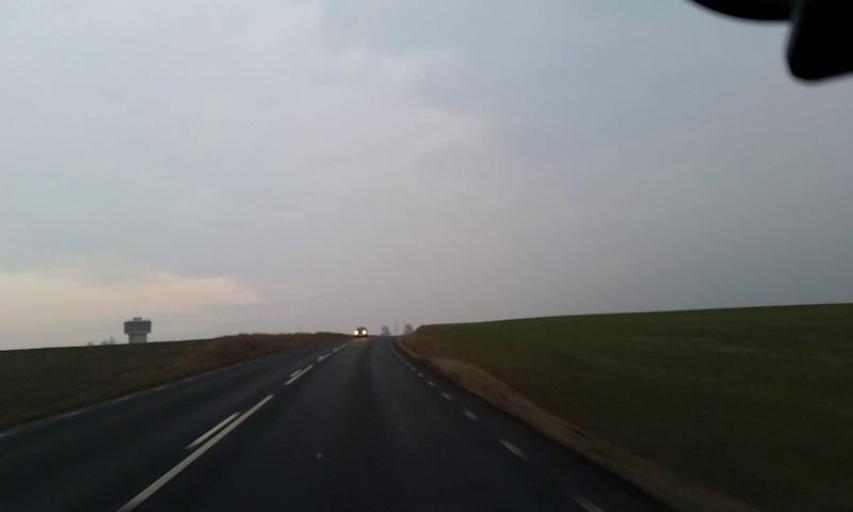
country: SE
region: Skane
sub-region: Angelholms Kommun
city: AEngelholm
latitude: 56.2640
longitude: 12.8881
